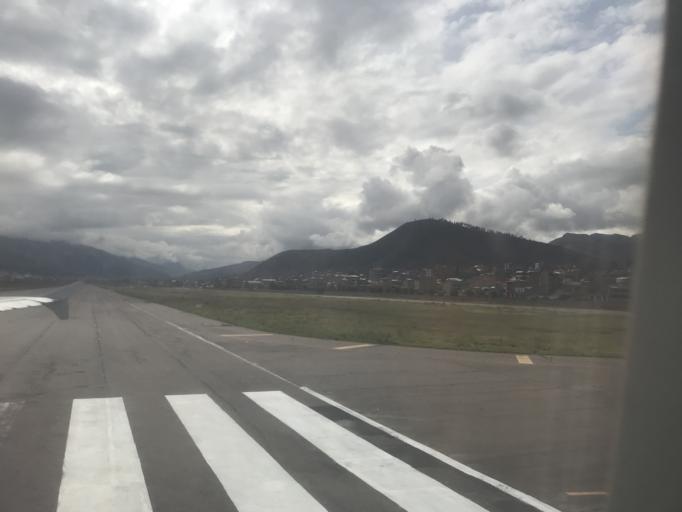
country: PE
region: Cusco
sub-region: Provincia de Cusco
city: Cusco
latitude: -13.5343
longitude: -71.9543
